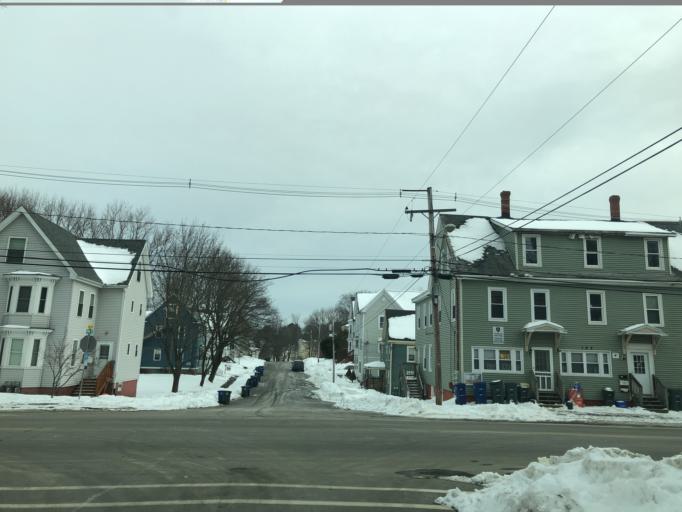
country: US
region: Maine
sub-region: Cumberland County
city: Westbrook
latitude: 43.6811
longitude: -70.3618
